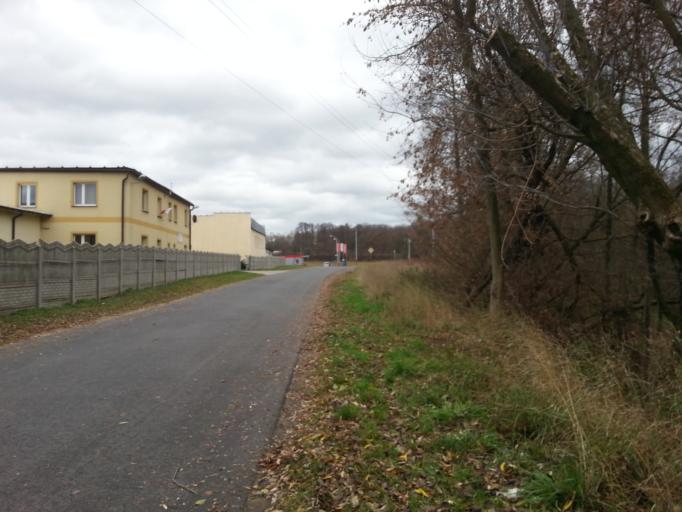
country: PL
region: Lower Silesian Voivodeship
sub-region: Powiat olesnicki
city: Twardogora
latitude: 51.3638
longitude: 17.4737
